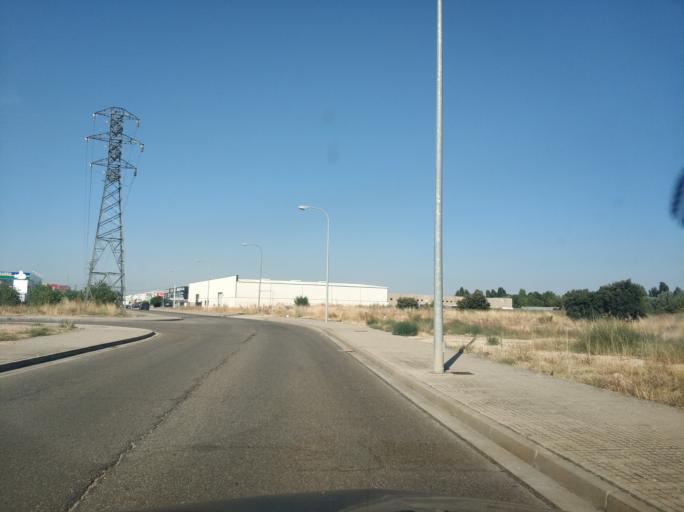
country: ES
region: Castille and Leon
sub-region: Provincia de Burgos
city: Aranda de Duero
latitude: 41.6723
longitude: -3.7020
